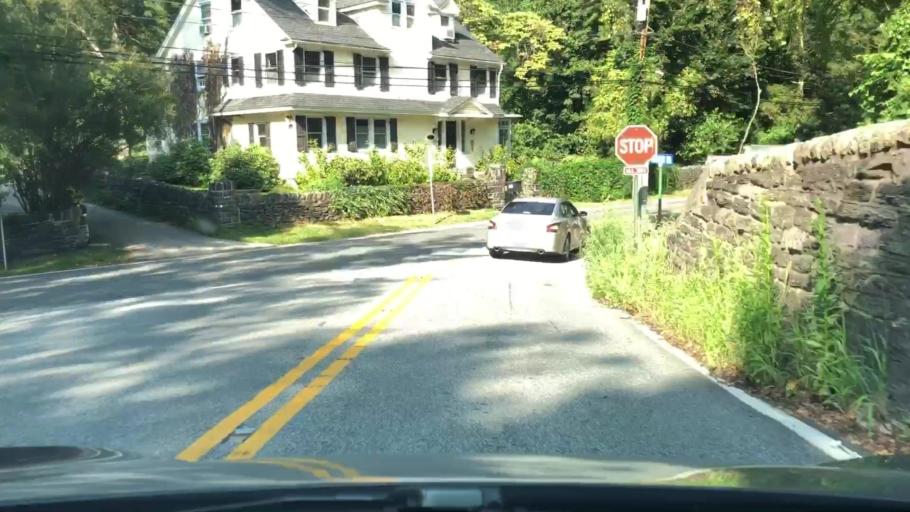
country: US
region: Pennsylvania
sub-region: Delaware County
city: Broomall
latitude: 40.0037
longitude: -75.3714
